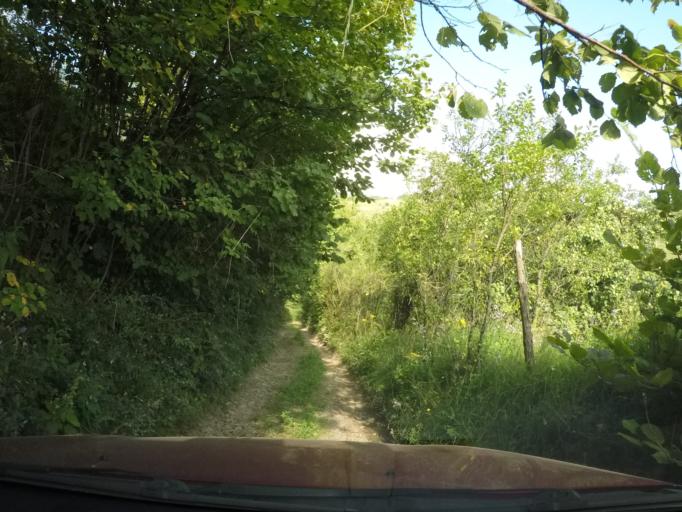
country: UA
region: Zakarpattia
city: Velykyi Bereznyi
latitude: 49.0236
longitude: 22.6379
